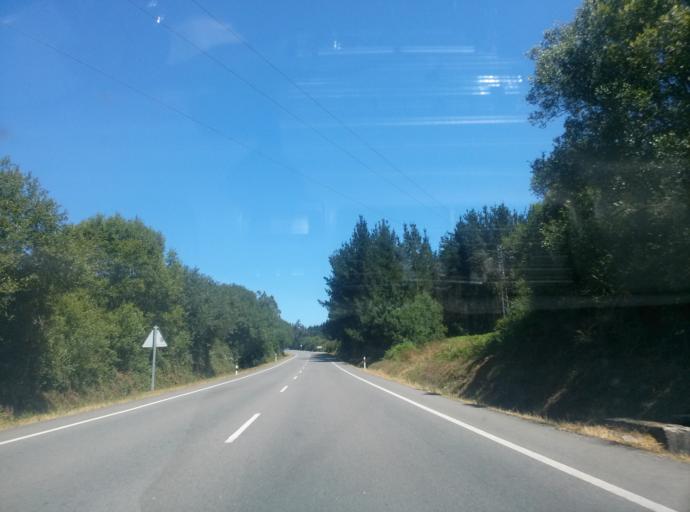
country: ES
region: Galicia
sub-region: Provincia de Lugo
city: Castro de Rei
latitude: 43.2312
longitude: -7.3695
